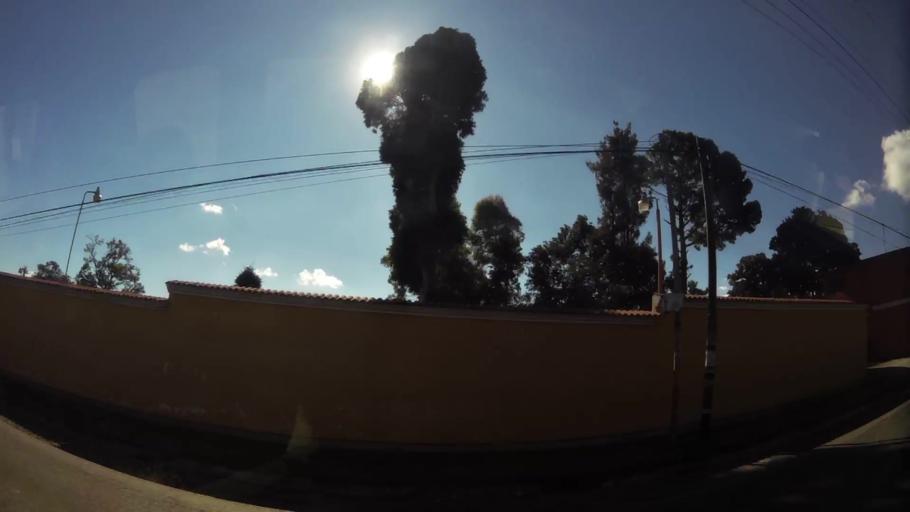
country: GT
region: Sacatepequez
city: Santa Lucia Milpas Altas
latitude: 14.5737
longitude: -90.6423
